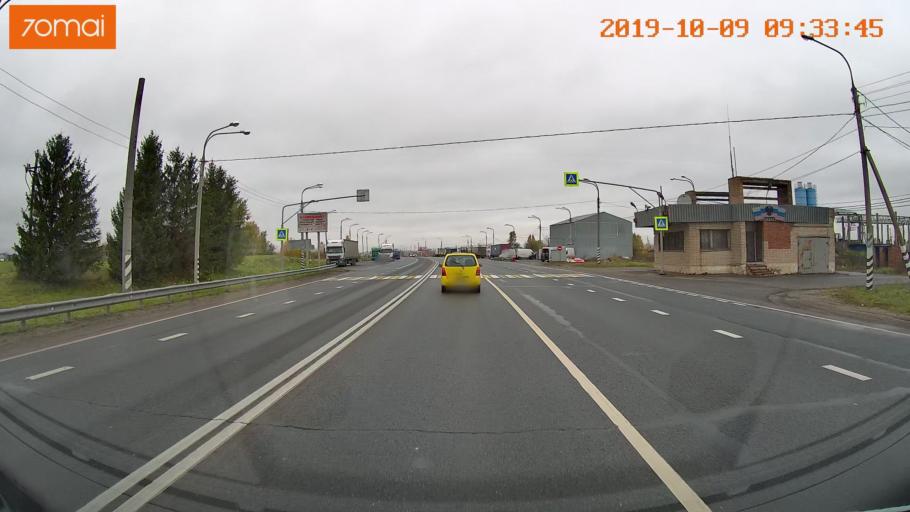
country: RU
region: Vologda
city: Vologda
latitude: 59.1708
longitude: 39.9090
